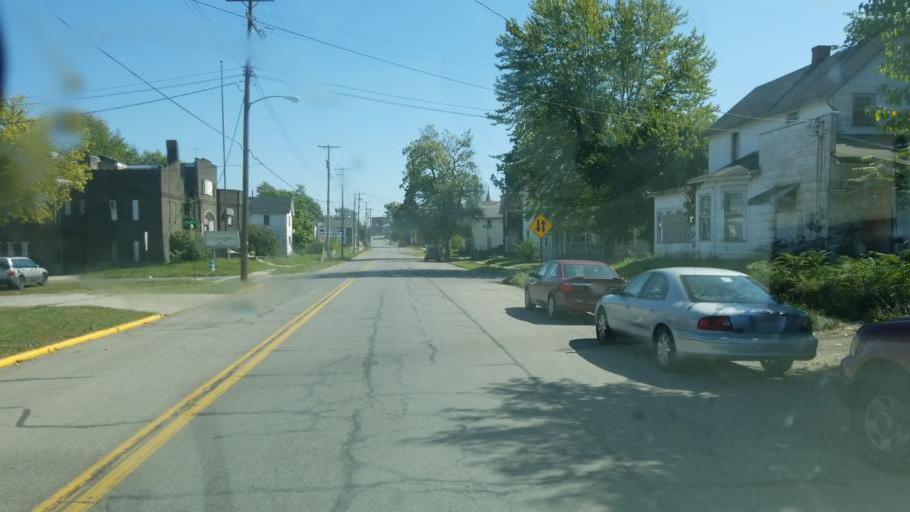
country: US
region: Ohio
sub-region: Marion County
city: Marion
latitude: 40.5870
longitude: -83.1385
